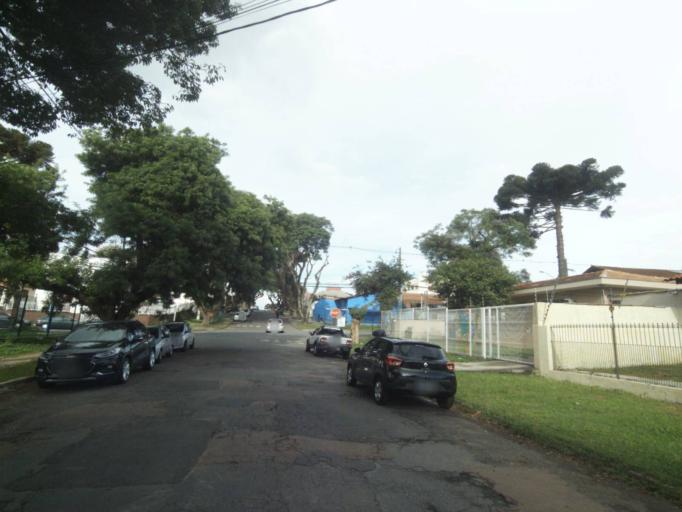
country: BR
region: Parana
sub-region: Curitiba
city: Curitiba
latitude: -25.4405
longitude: -49.3095
